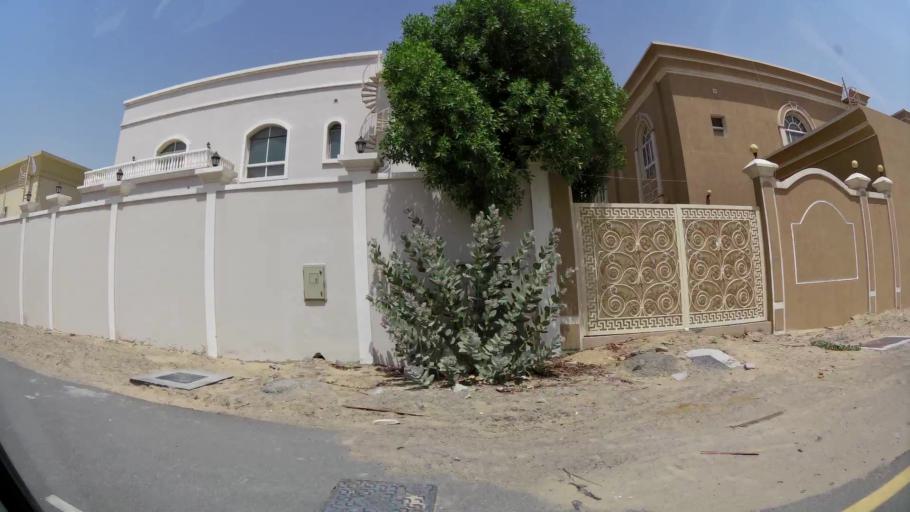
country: AE
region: Ash Shariqah
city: Sharjah
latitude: 25.2543
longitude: 55.5033
